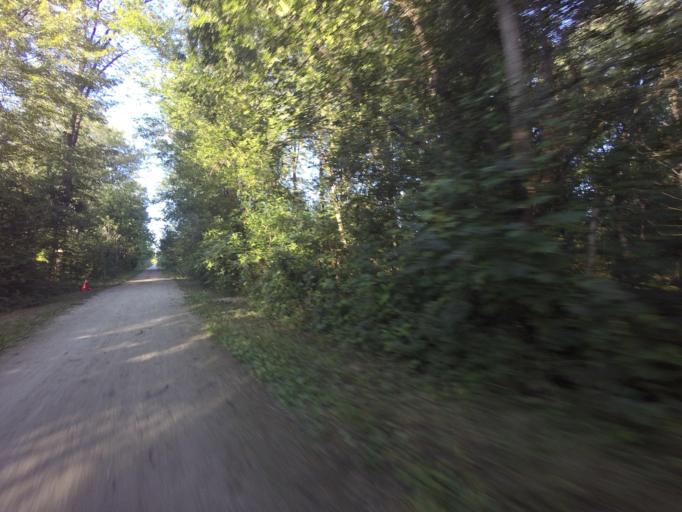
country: CA
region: Ontario
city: Orangeville
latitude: 43.8135
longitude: -79.9295
